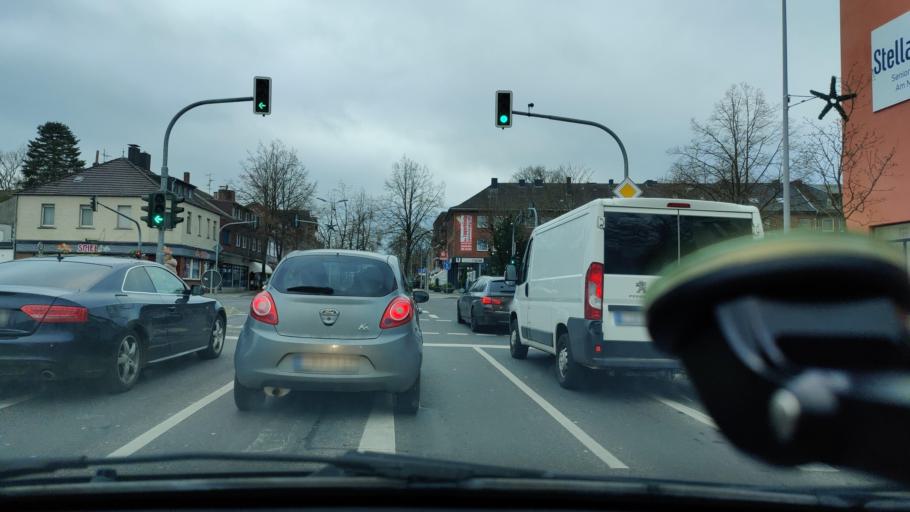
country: DE
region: North Rhine-Westphalia
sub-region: Regierungsbezirk Koln
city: Alsdorf
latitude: 50.8589
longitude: 6.2029
